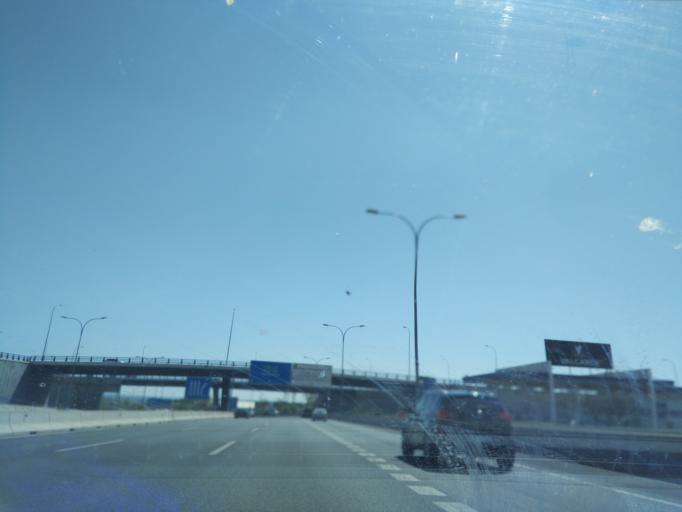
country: ES
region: Madrid
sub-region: Provincia de Madrid
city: Villa de Vallecas
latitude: 40.3686
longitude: -3.5871
